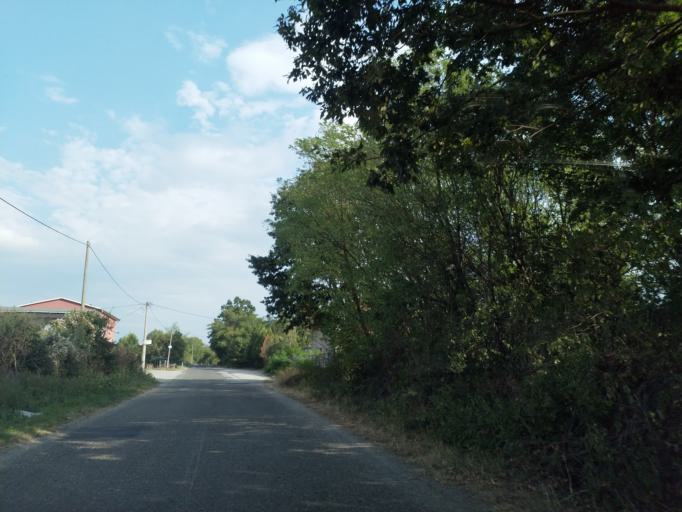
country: RS
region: Central Serbia
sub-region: Pomoravski Okrug
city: Paracin
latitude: 43.8535
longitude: 21.4426
